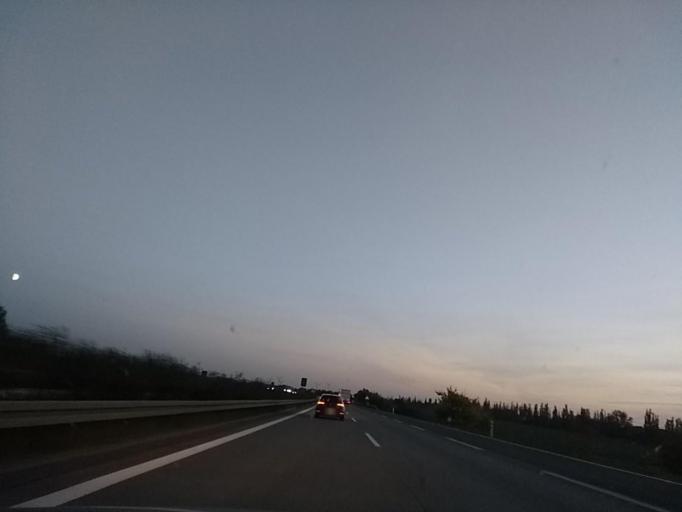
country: DE
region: Mecklenburg-Vorpommern
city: Roggentin
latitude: 54.0764
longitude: 12.1949
